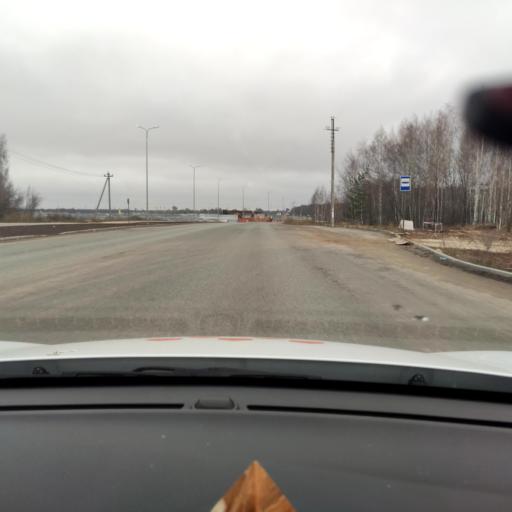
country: RU
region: Tatarstan
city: Osinovo
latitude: 55.8544
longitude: 48.9084
